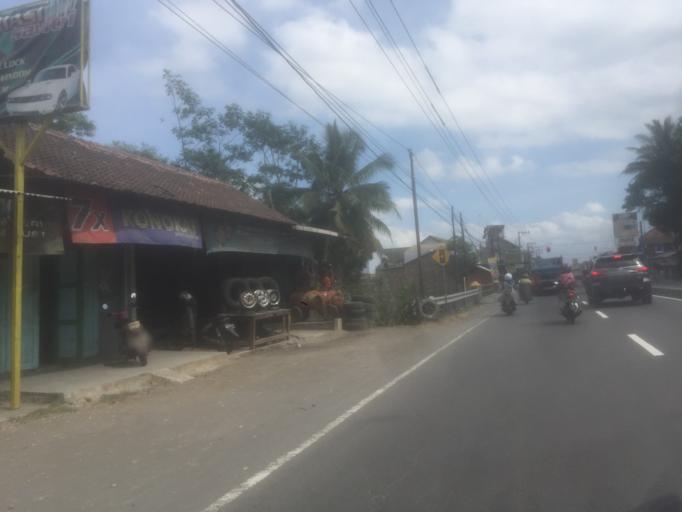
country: ID
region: Central Java
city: Muntilan
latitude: -7.5988
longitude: 110.2966
